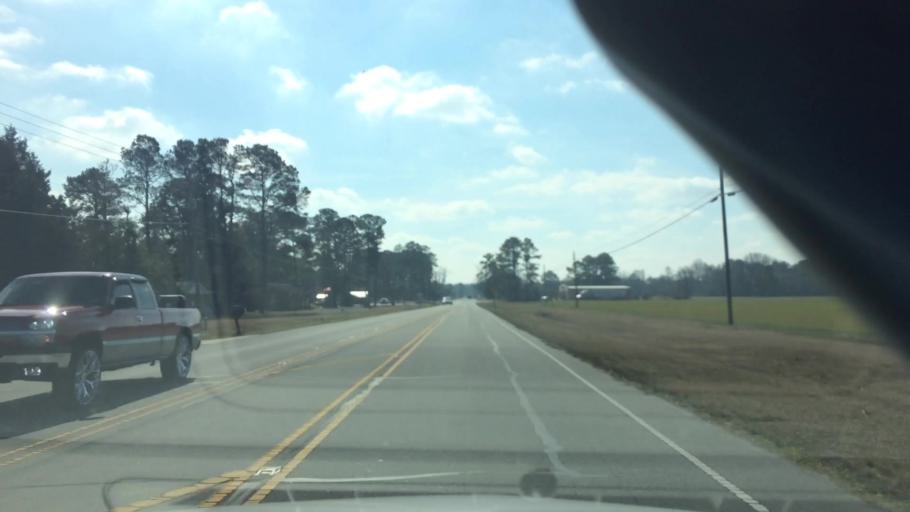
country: US
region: North Carolina
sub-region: Duplin County
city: Beulaville
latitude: 35.0713
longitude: -77.7361
